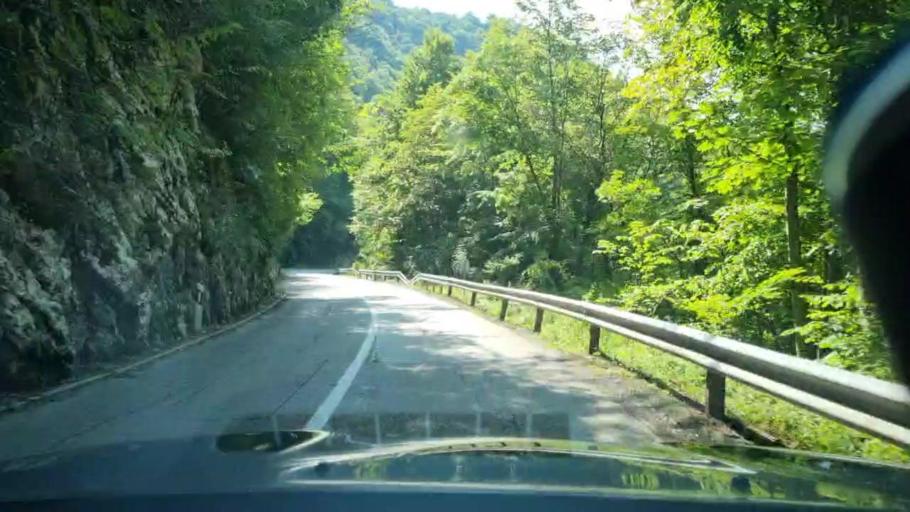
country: BA
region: Federation of Bosnia and Herzegovina
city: Bosanska Krupa
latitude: 44.8724
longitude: 16.0824
